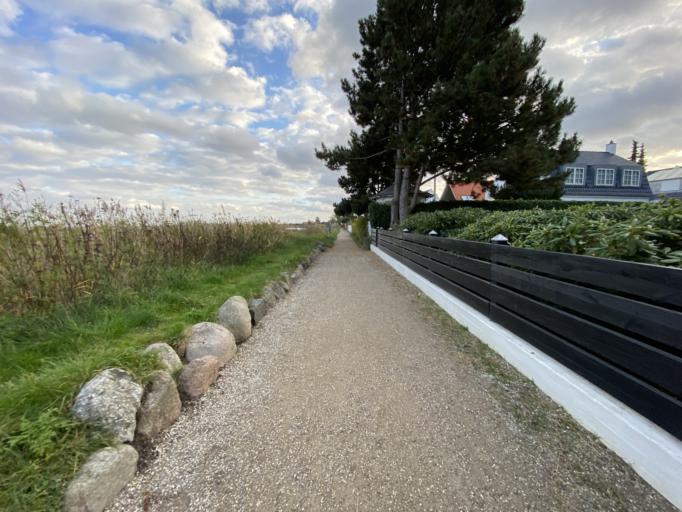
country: DK
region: Capital Region
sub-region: Dragor Kommune
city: Dragor
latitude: 55.5998
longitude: 12.6717
